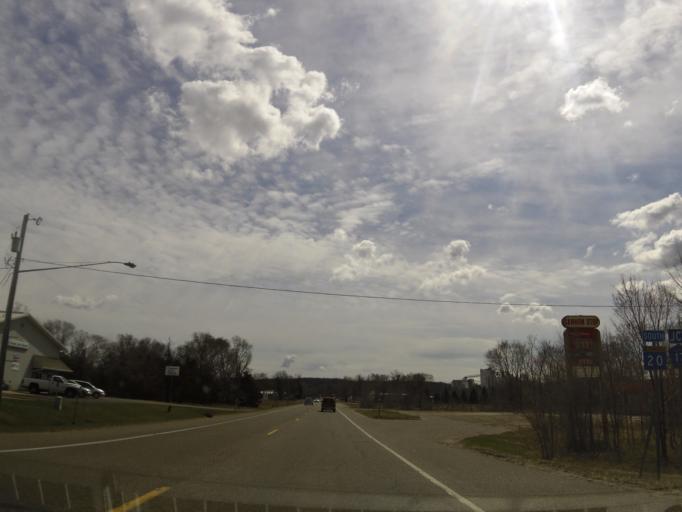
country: US
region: Minnesota
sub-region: Goodhue County
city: Cannon Falls
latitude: 44.5238
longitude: -92.9109
